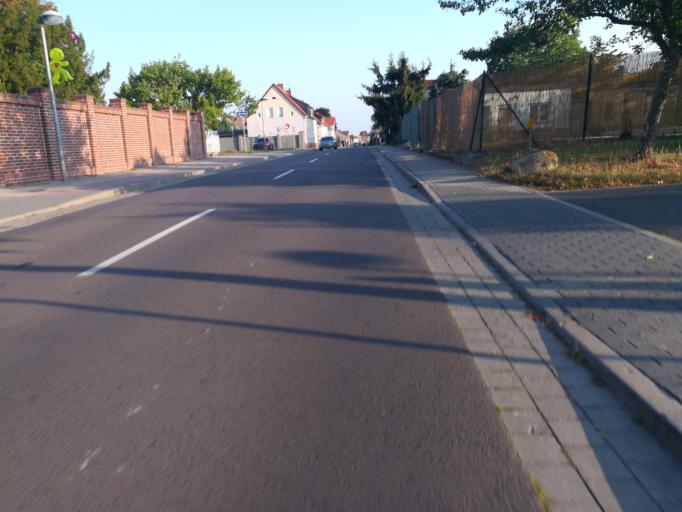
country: DE
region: Saxony-Anhalt
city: Irxleben
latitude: 52.1612
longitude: 11.4851
